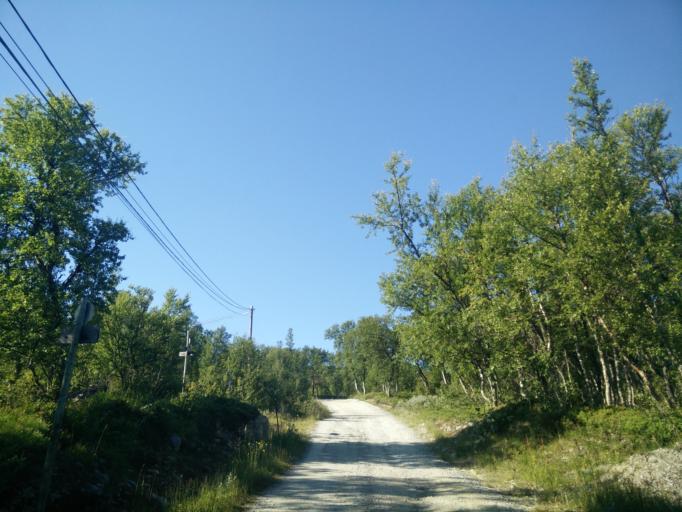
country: NO
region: Sor-Trondelag
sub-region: Tydal
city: Aas
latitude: 62.5762
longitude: 12.2012
